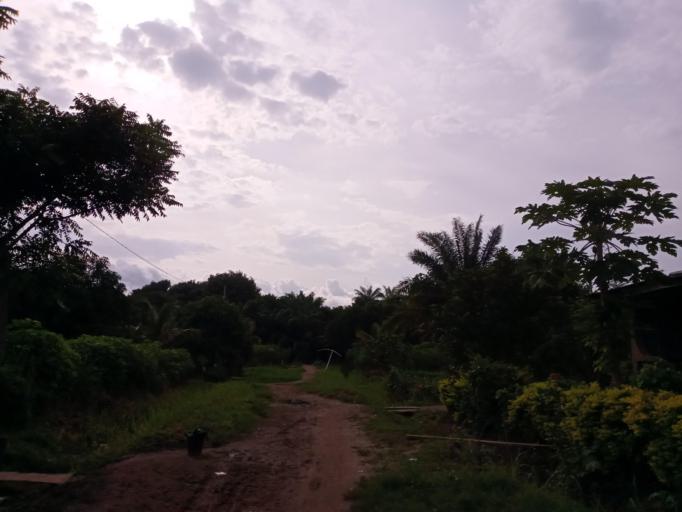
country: SL
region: Northern Province
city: Bumbuna
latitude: 9.0501
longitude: -11.7567
